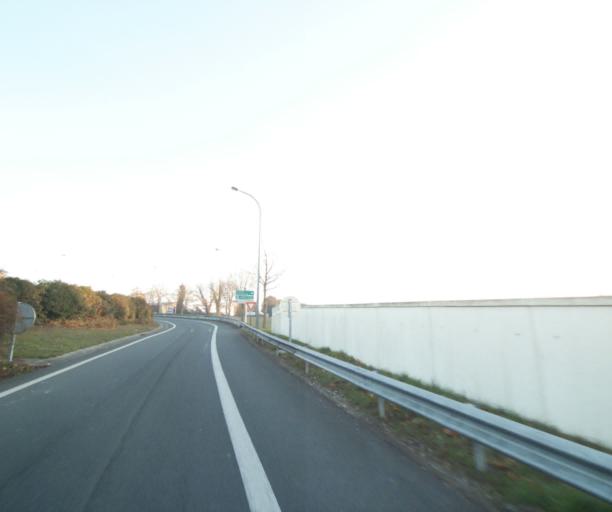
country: FR
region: Poitou-Charentes
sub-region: Departement de la Charente-Maritime
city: Fontcouverte
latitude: 45.7447
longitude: -0.5996
